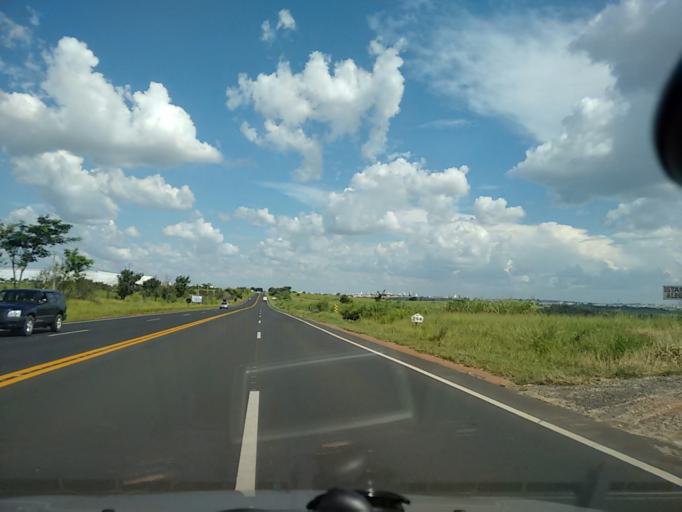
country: BR
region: Sao Paulo
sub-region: Marilia
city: Marilia
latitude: -22.1636
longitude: -49.9935
